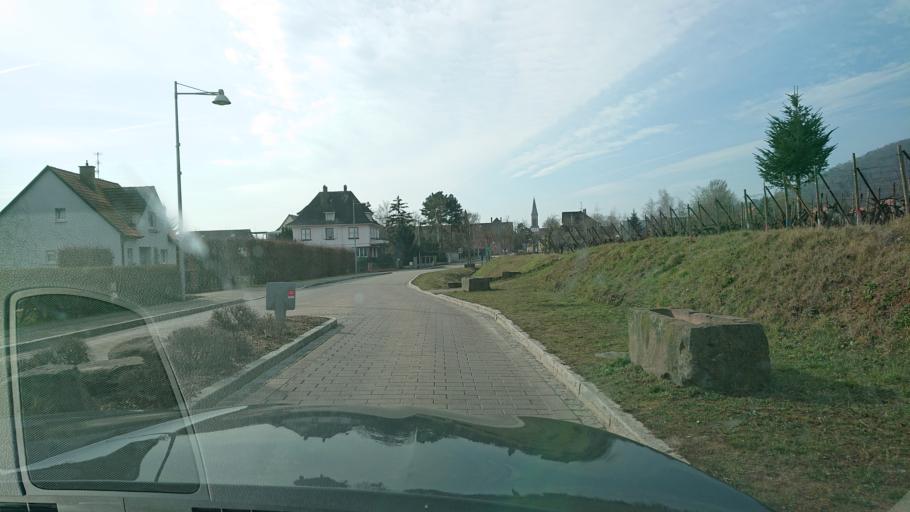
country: FR
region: Alsace
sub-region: Departement du Bas-Rhin
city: Kintzheim
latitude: 48.2592
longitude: 7.3979
